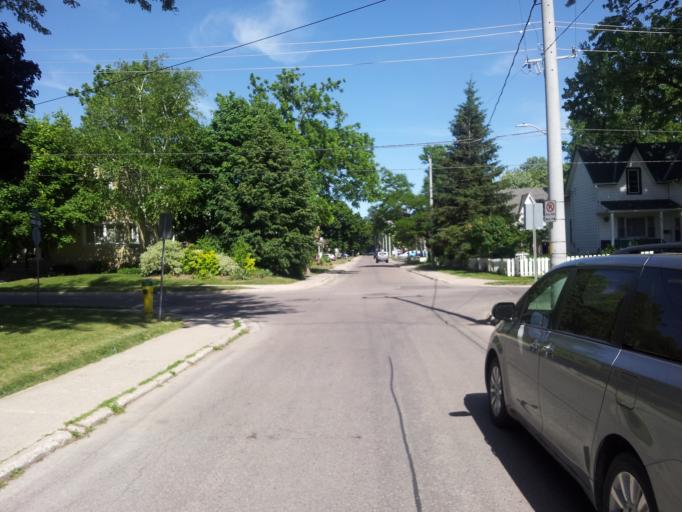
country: CA
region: Ontario
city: Stratford
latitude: 43.3690
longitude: -80.9772
